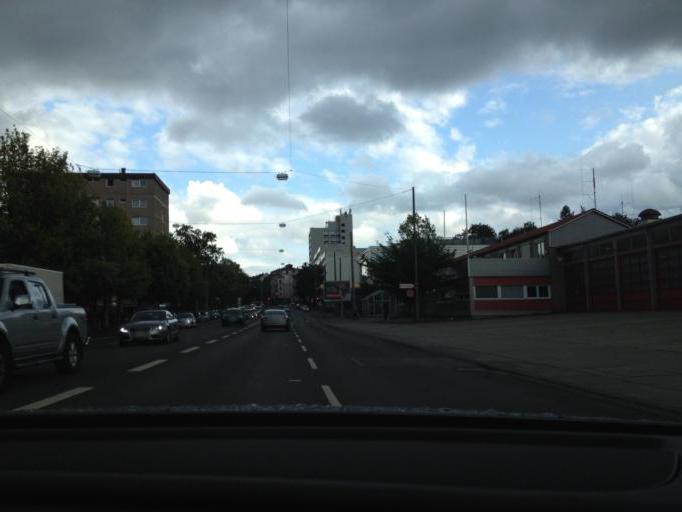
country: DE
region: Hesse
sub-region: Regierungsbezirk Darmstadt
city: Wiesbaden
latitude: 50.0801
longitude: 8.2189
